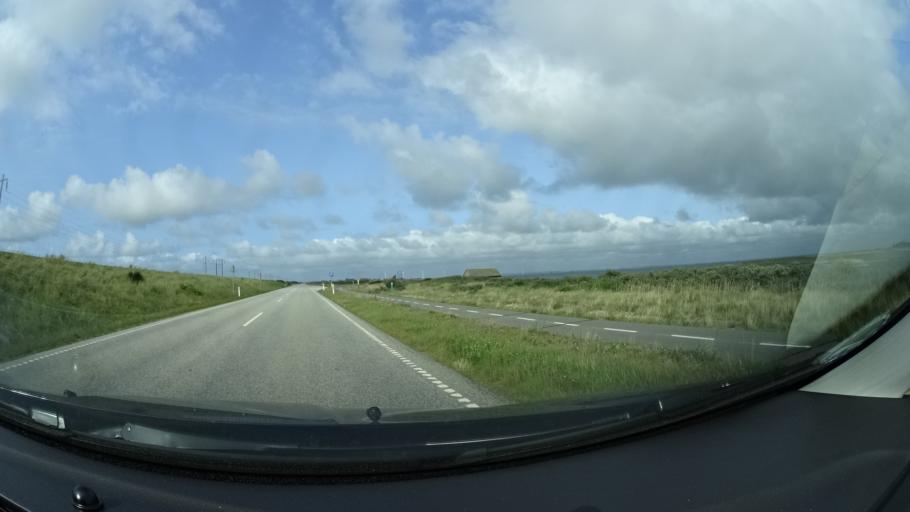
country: DK
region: Central Jutland
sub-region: Lemvig Kommune
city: Harboore
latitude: 56.6326
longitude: 8.1847
